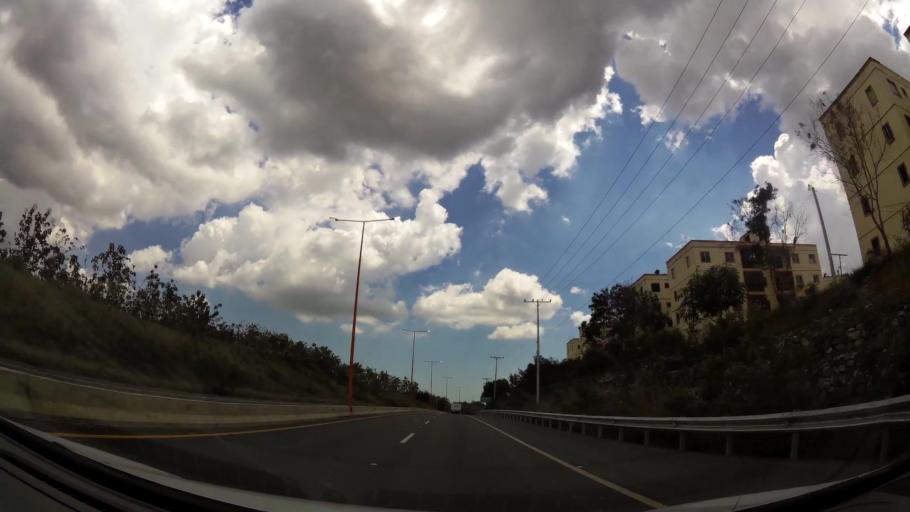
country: DO
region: Nacional
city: Santo Domingo
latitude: 18.5649
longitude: -69.9785
